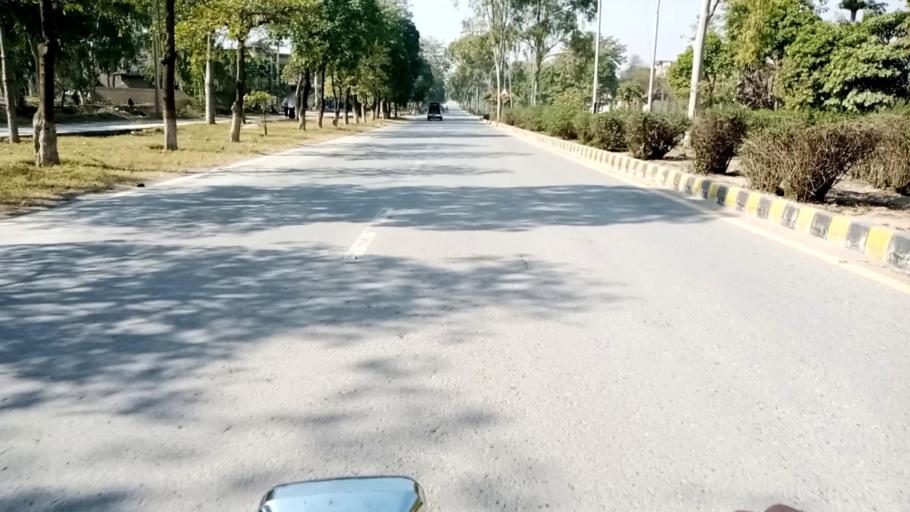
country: PK
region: Khyber Pakhtunkhwa
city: Peshawar
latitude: 33.9564
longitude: 71.4301
